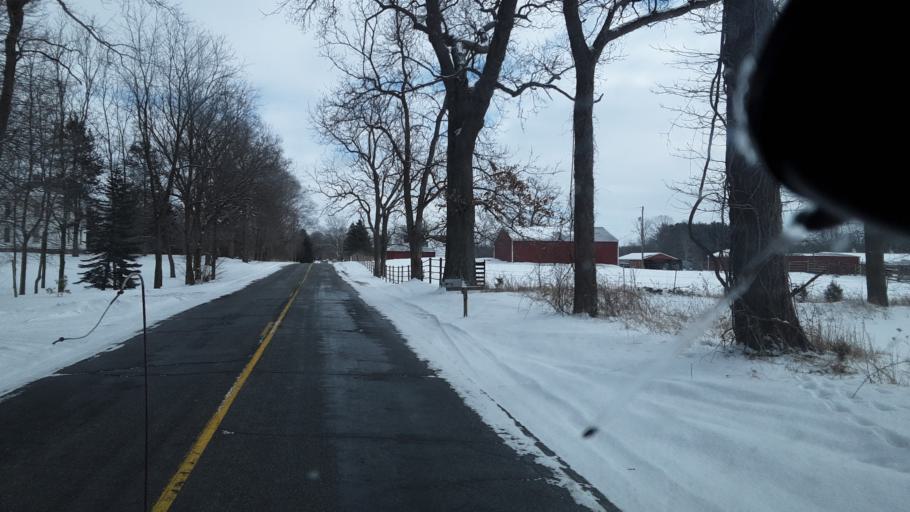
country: US
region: Michigan
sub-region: Ingham County
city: Leslie
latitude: 42.4753
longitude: -84.3223
